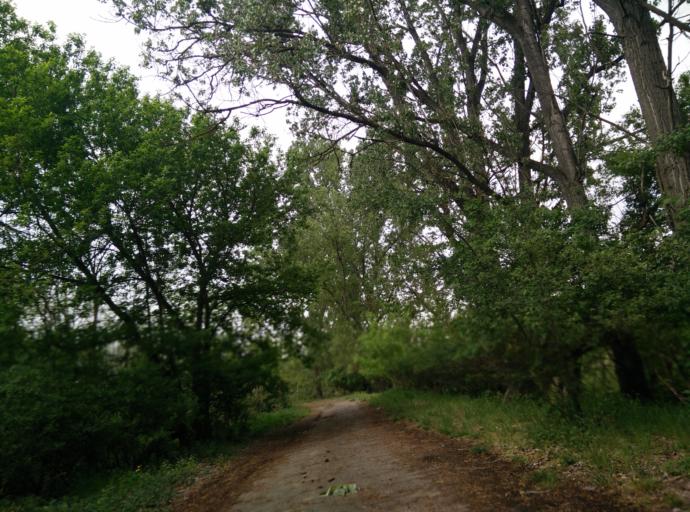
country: HU
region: Pest
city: Fot
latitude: 47.6006
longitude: 19.1539
